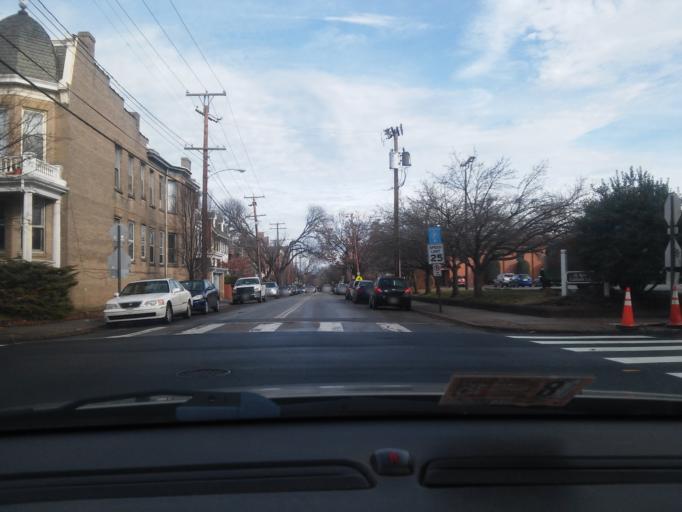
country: US
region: Virginia
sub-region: City of Richmond
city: Richmond
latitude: 37.5574
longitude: -77.4776
